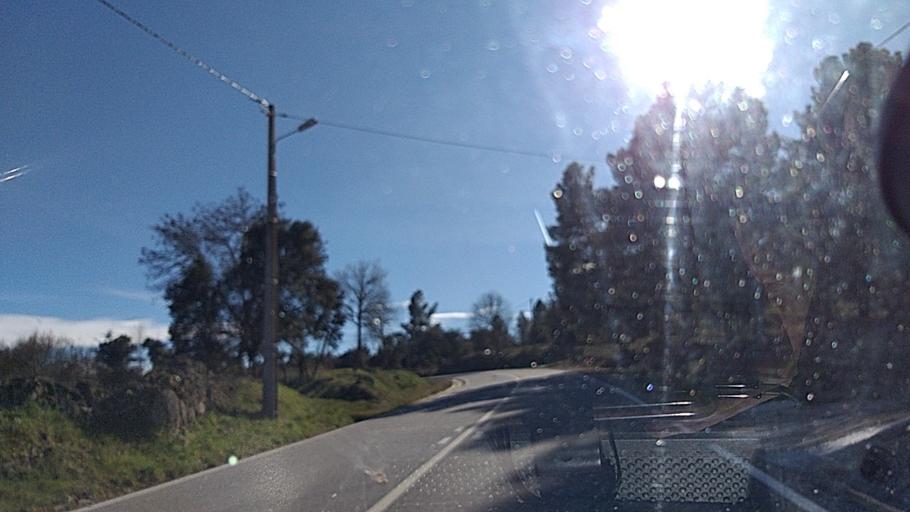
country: ES
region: Castille and Leon
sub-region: Provincia de Salamanca
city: Fuentes de Onoro
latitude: 40.6160
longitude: -6.8927
